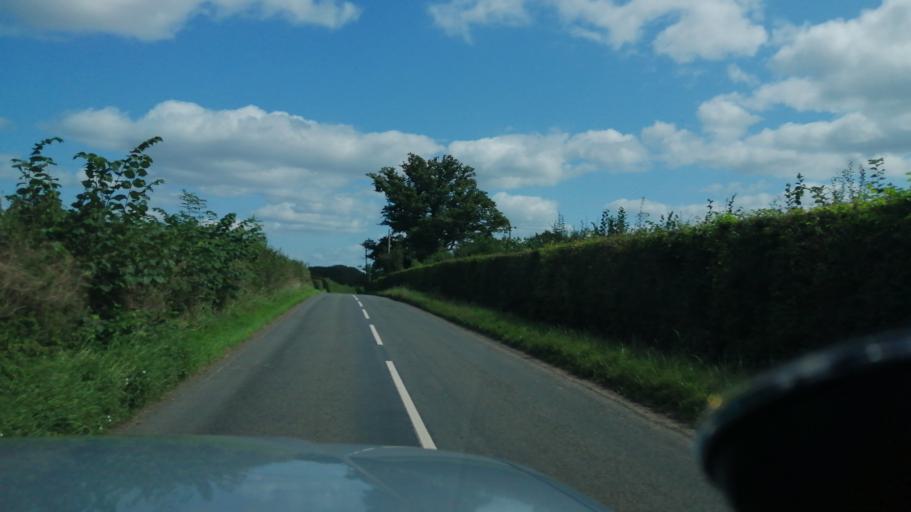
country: GB
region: England
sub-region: Herefordshire
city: Moccas
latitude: 52.0766
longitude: -2.9401
